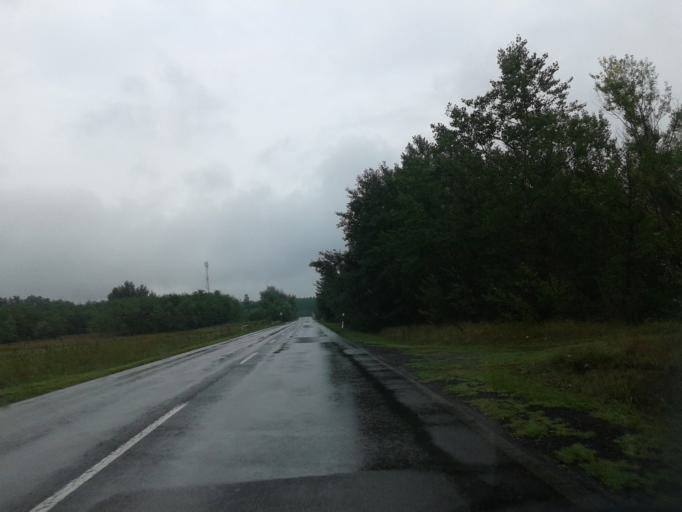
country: HU
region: Bacs-Kiskun
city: Kelebia
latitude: 46.2535
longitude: 19.6533
